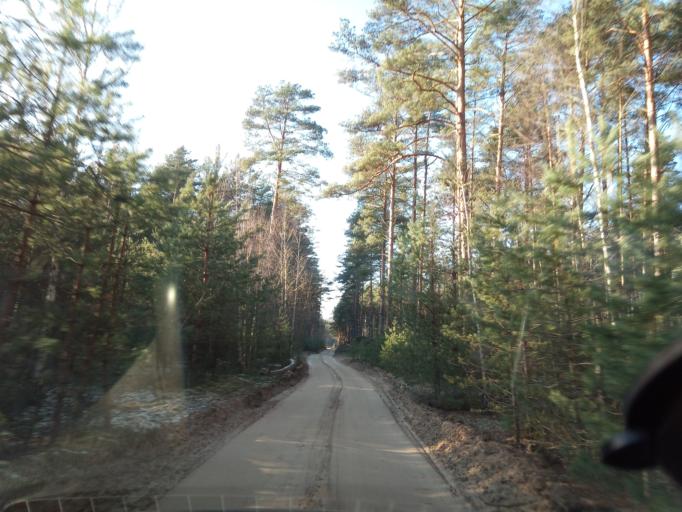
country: LT
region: Alytaus apskritis
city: Druskininkai
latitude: 53.9568
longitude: 23.8693
